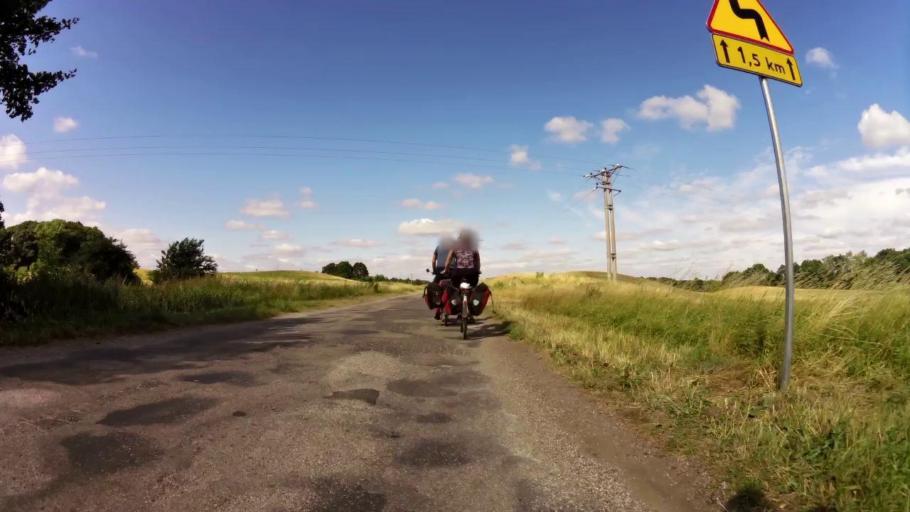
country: PL
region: West Pomeranian Voivodeship
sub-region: Powiat lobeski
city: Lobez
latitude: 53.6451
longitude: 15.6707
